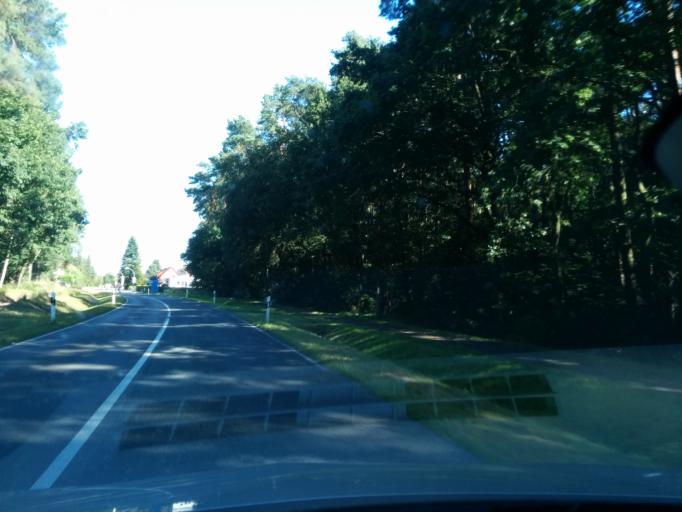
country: DE
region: Mecklenburg-Vorpommern
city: Torgelow
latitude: 53.6323
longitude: 13.9906
